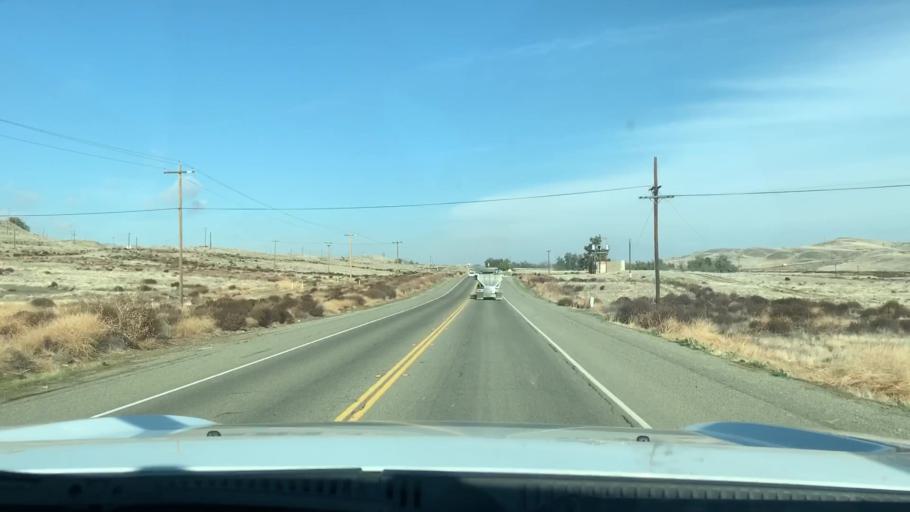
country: US
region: California
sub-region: Fresno County
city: Coalinga
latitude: 36.2411
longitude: -120.3148
